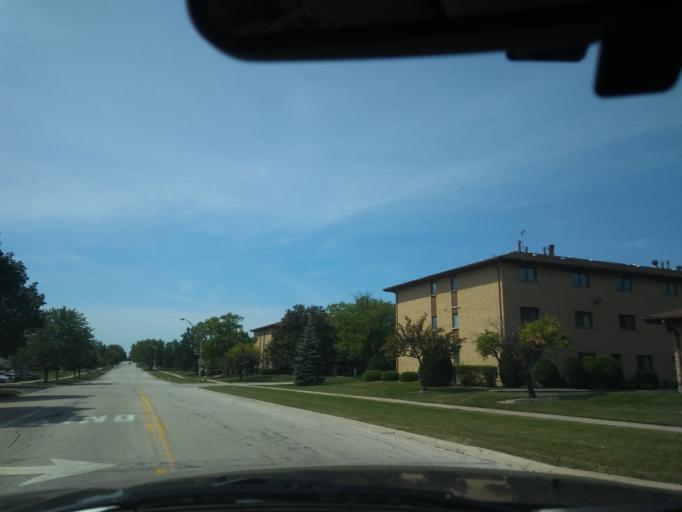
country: US
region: Illinois
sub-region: Cook County
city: Tinley Park
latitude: 41.6169
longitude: -87.7968
